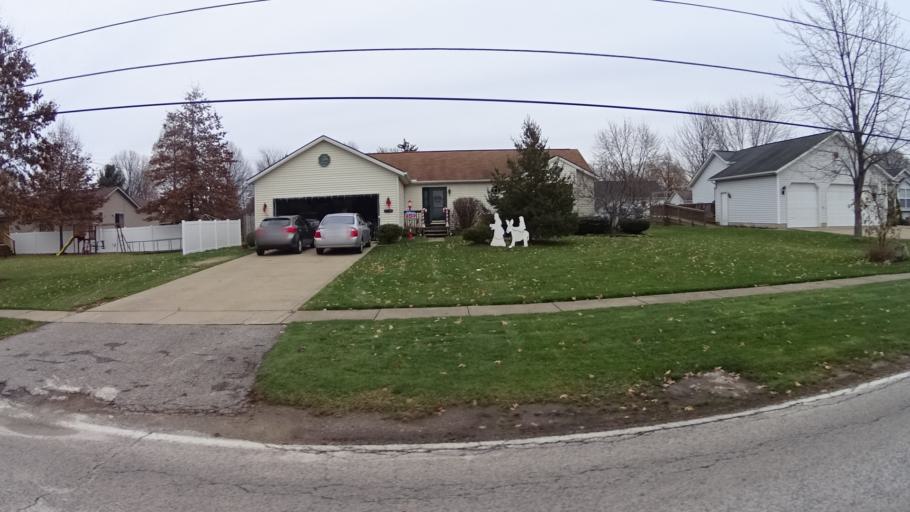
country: US
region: Ohio
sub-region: Lorain County
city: North Ridgeville
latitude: 41.3598
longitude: -81.9914
